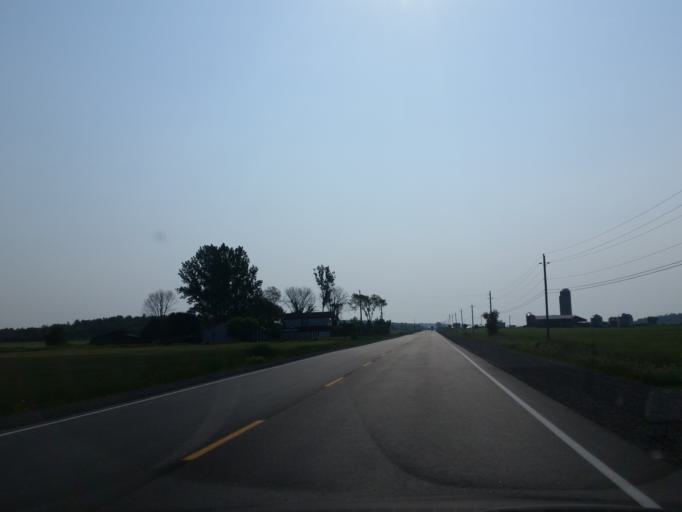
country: CA
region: Ontario
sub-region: Nipissing District
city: North Bay
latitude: 46.4070
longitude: -80.0808
